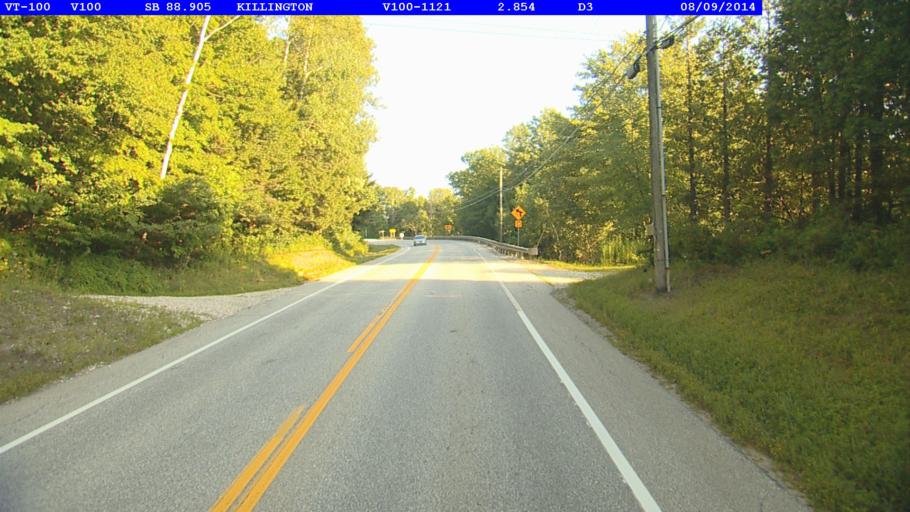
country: US
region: Vermont
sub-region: Rutland County
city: Rutland
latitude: 43.7030
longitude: -72.8223
